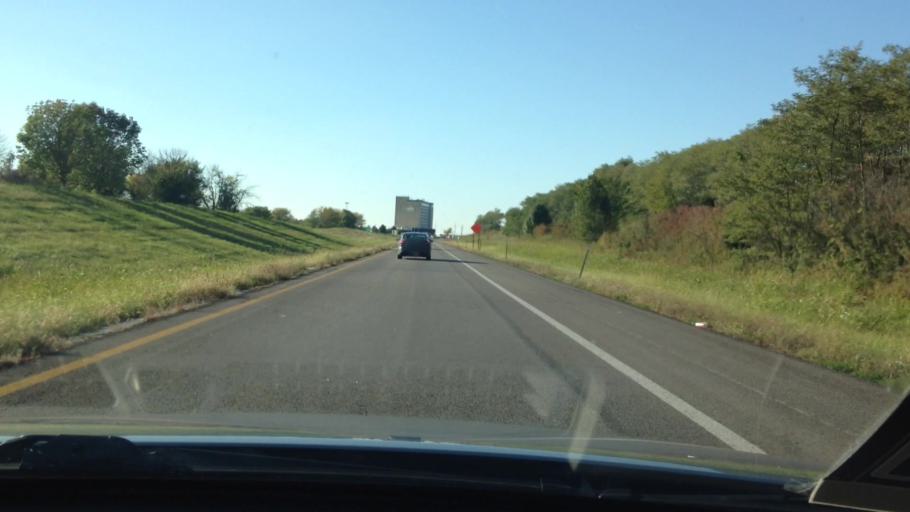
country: US
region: Missouri
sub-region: Platte County
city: Weatherby Lake
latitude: 39.2553
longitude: -94.6537
